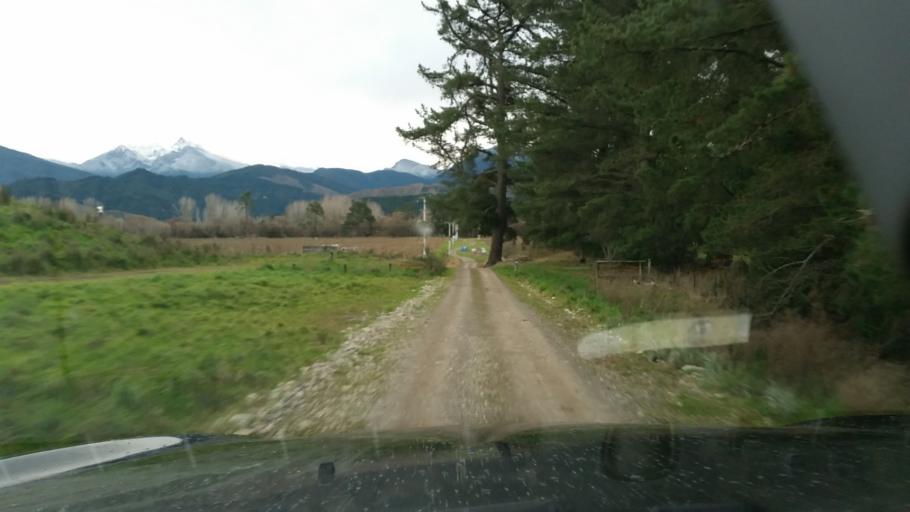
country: NZ
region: Nelson
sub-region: Nelson City
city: Nelson
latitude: -41.5607
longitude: 173.5213
